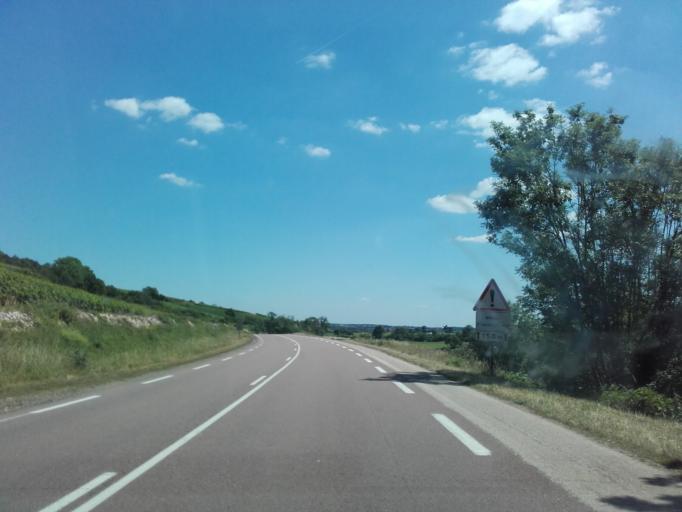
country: FR
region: Bourgogne
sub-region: Departement de la Cote-d'Or
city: Corpeau
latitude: 46.9492
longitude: 4.7265
